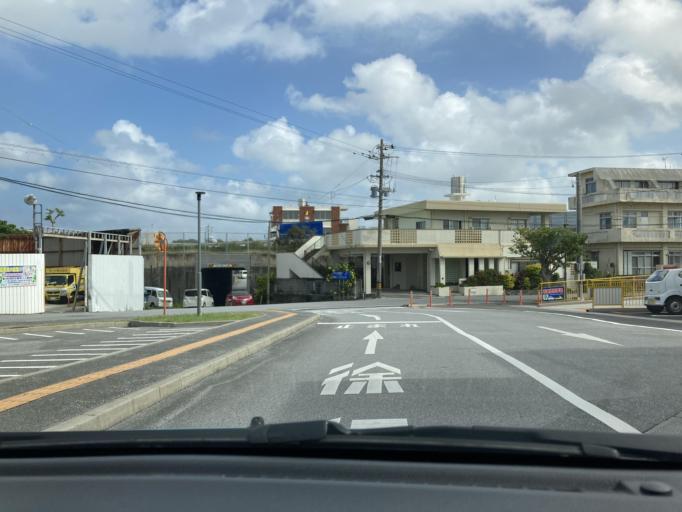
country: JP
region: Okinawa
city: Ginowan
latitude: 26.2536
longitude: 127.7360
